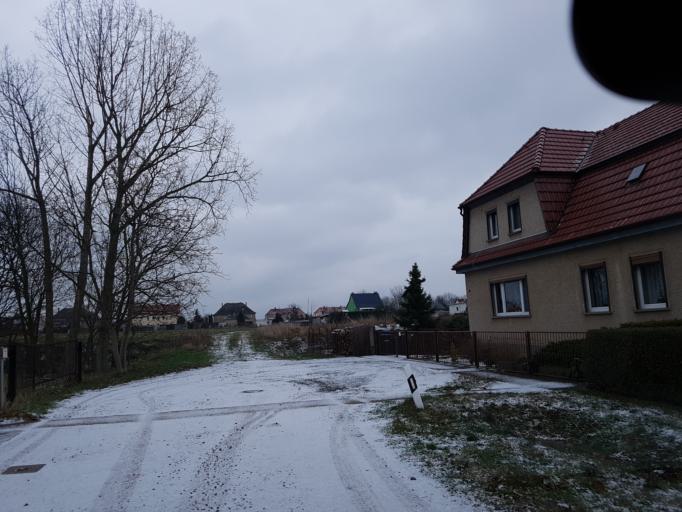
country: DE
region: Brandenburg
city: Muhlberg
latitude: 51.4320
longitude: 13.2218
